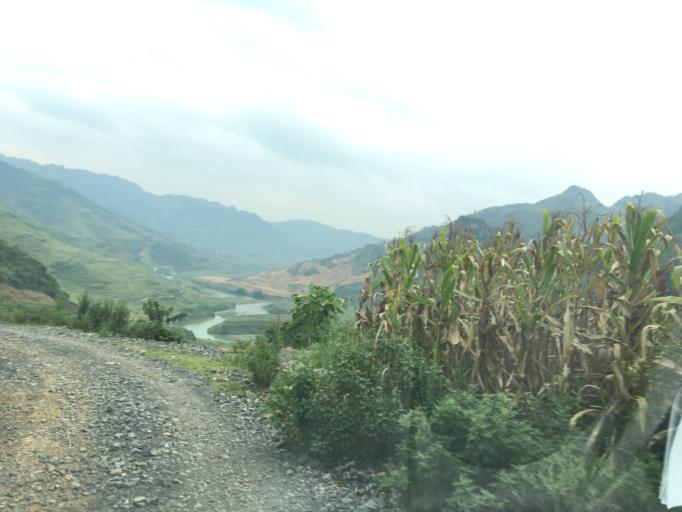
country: CN
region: Guangxi Zhuangzu Zizhiqu
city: Xinzhou
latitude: 25.1745
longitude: 105.7320
